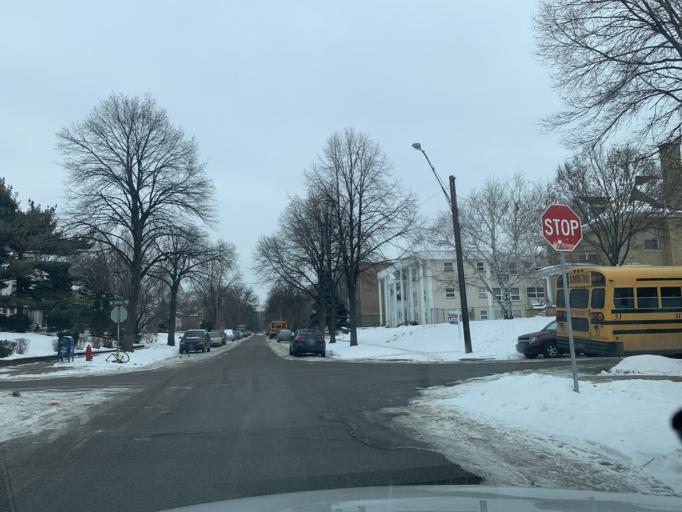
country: US
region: Minnesota
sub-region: Hennepin County
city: Minneapolis
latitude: 44.9572
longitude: -93.2813
